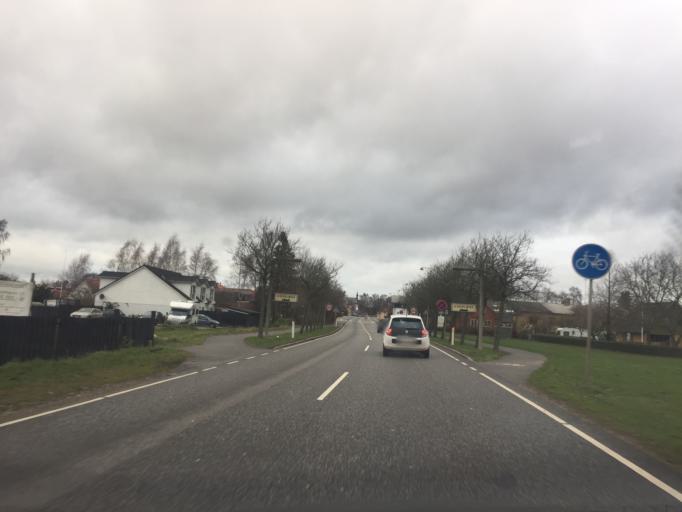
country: DK
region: Zealand
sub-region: Soro Kommune
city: Stenlille
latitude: 55.5814
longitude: 11.6541
